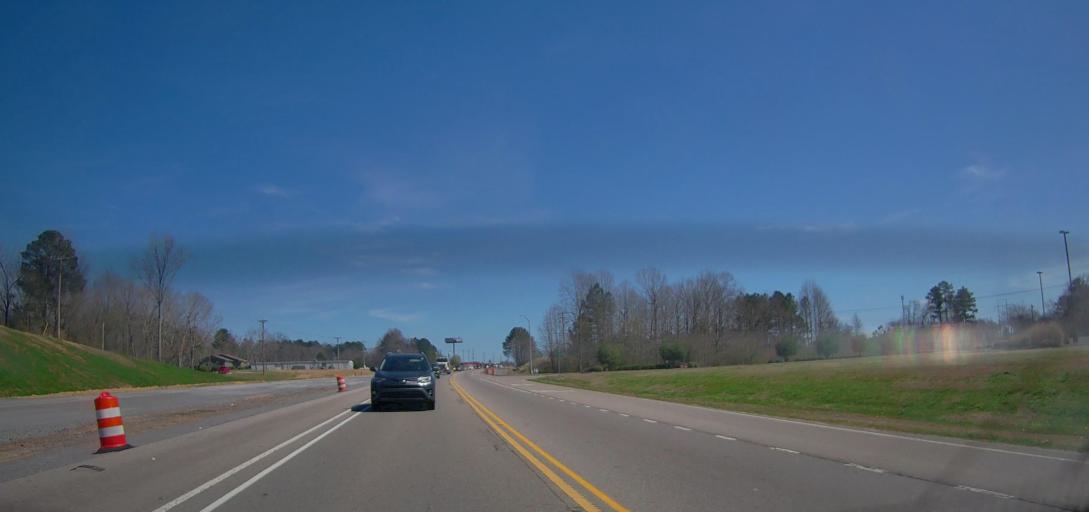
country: US
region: Alabama
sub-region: Cullman County
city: Cullman
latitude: 34.2055
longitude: -86.8359
